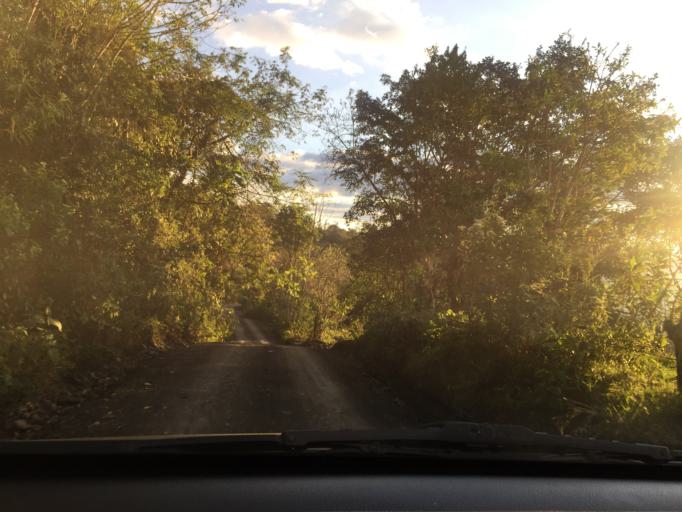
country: CO
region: Cundinamarca
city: Zipacon
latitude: 4.7114
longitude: -74.3976
